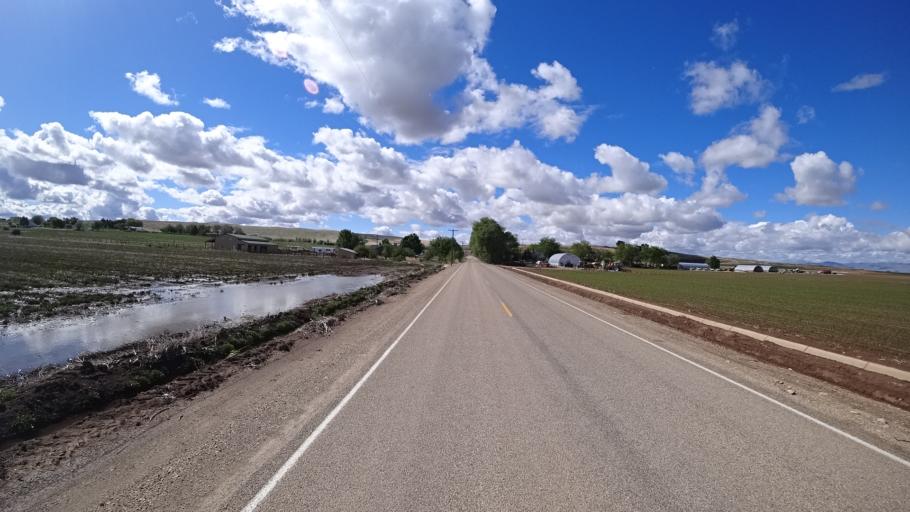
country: US
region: Idaho
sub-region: Ada County
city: Kuna
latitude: 43.4674
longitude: -116.4736
